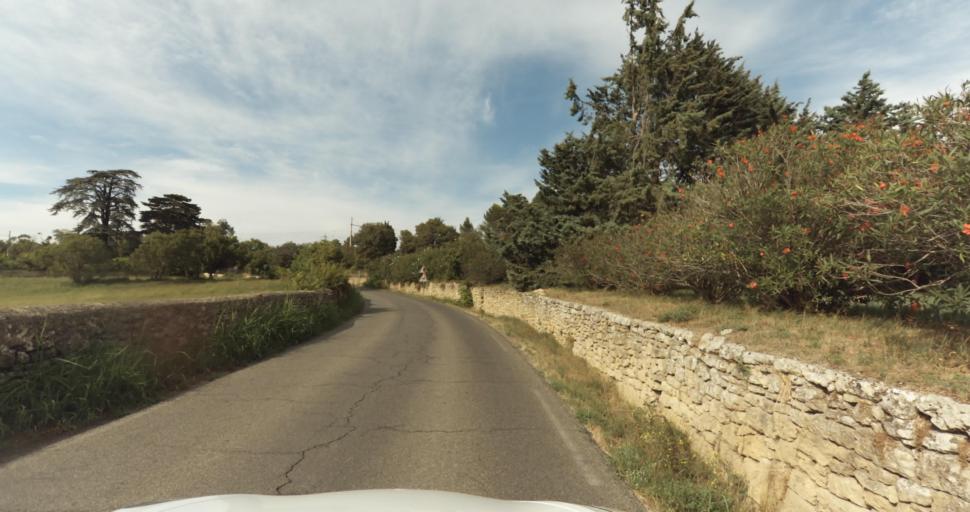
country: FR
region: Provence-Alpes-Cote d'Azur
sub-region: Departement des Bouches-du-Rhone
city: Miramas
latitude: 43.5744
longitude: 5.0223
